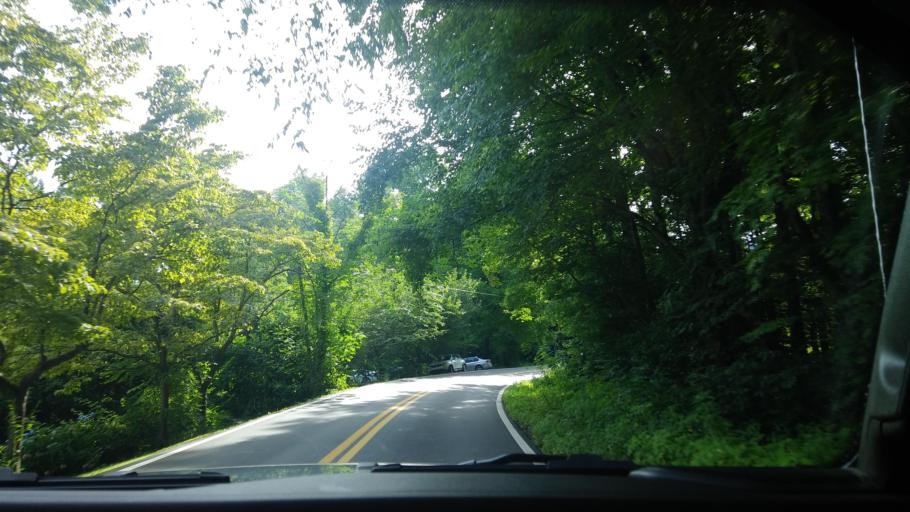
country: US
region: Tennessee
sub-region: Cocke County
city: Newport
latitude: 35.7847
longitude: -83.1912
